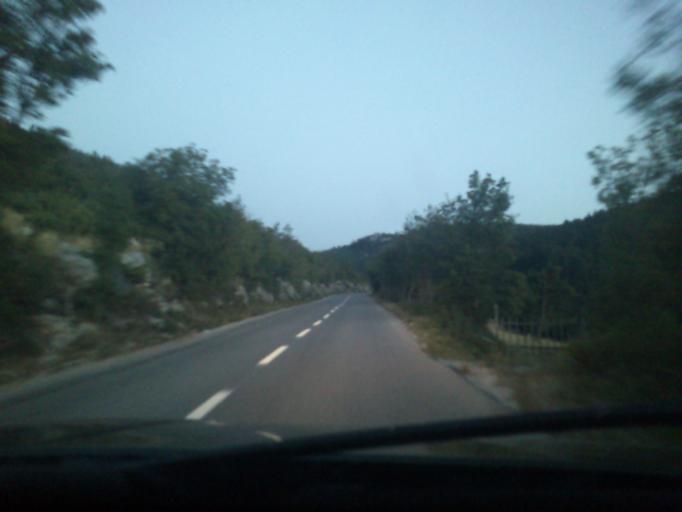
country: HR
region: Licko-Senjska
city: Senj
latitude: 44.8906
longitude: 14.9639
